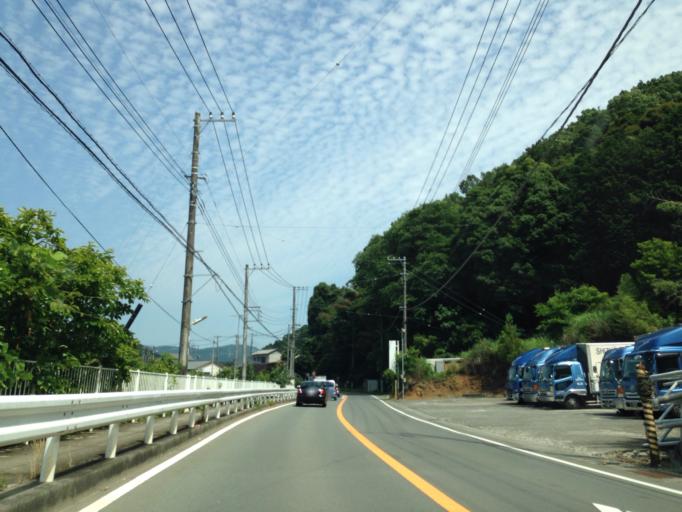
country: JP
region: Shizuoka
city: Numazu
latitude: 35.0252
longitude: 138.9189
